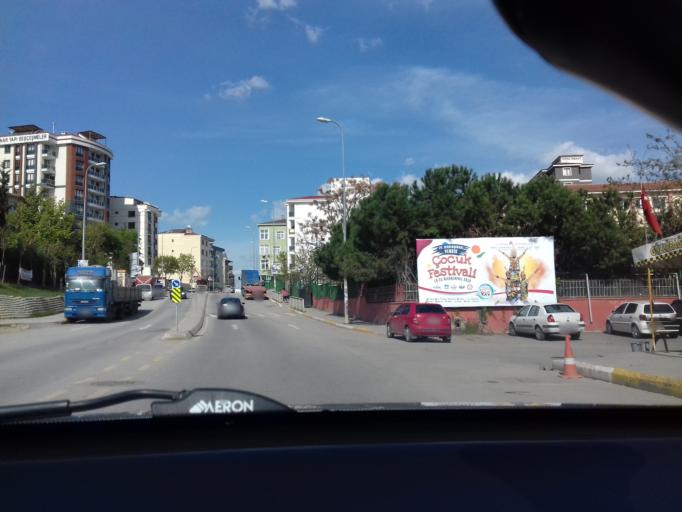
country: TR
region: Istanbul
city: Pendik
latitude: 40.8940
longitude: 29.2733
